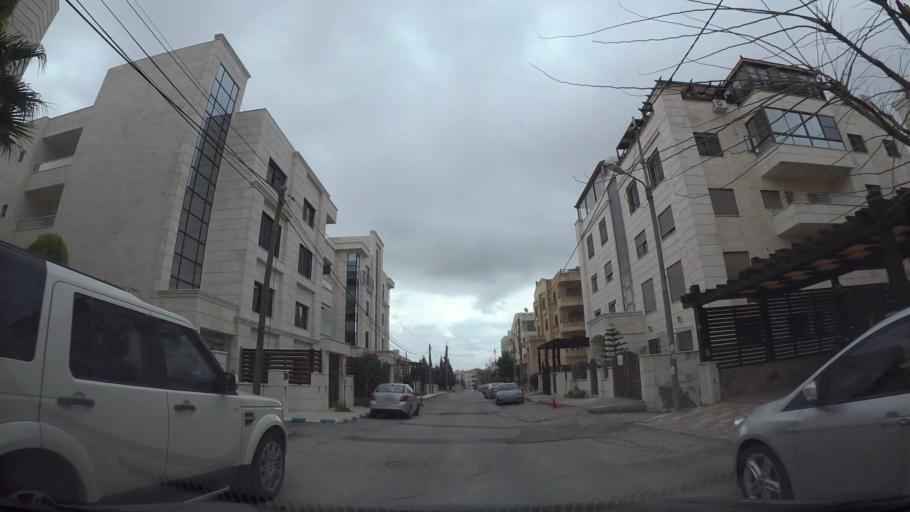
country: JO
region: Amman
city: Wadi as Sir
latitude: 31.9626
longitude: 35.8273
